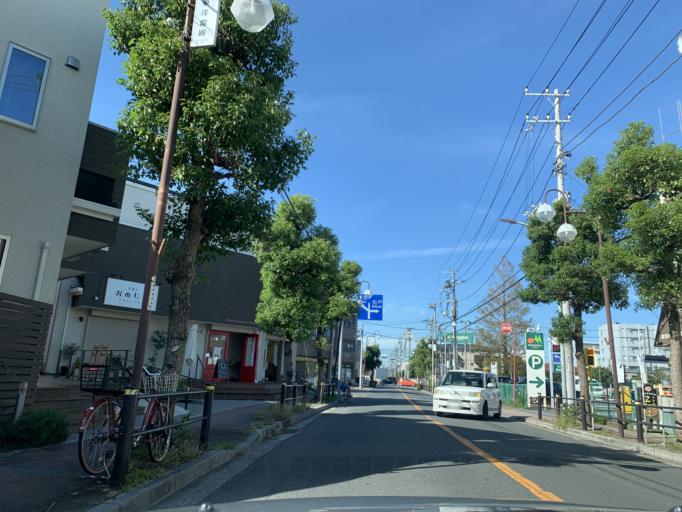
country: JP
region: Chiba
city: Matsudo
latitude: 35.7313
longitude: 139.9220
